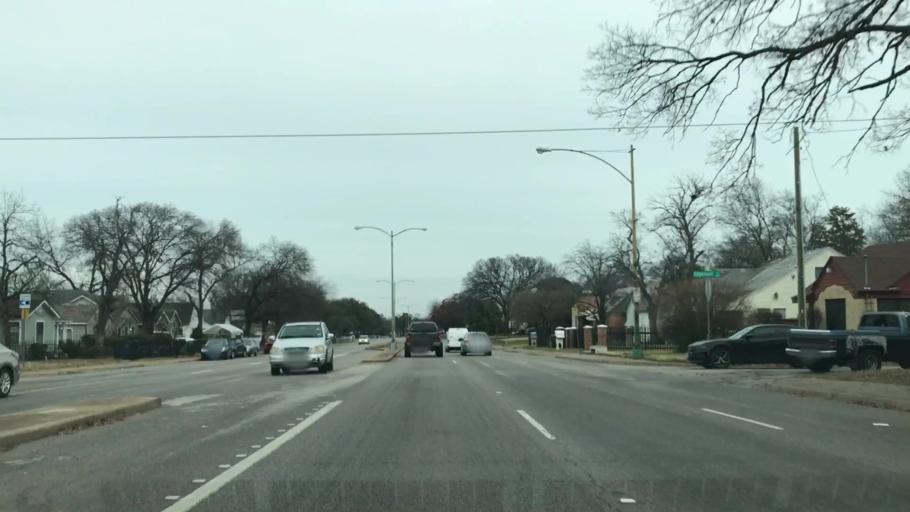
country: US
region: Texas
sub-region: Dallas County
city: Dallas
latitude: 32.7294
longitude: -96.8144
